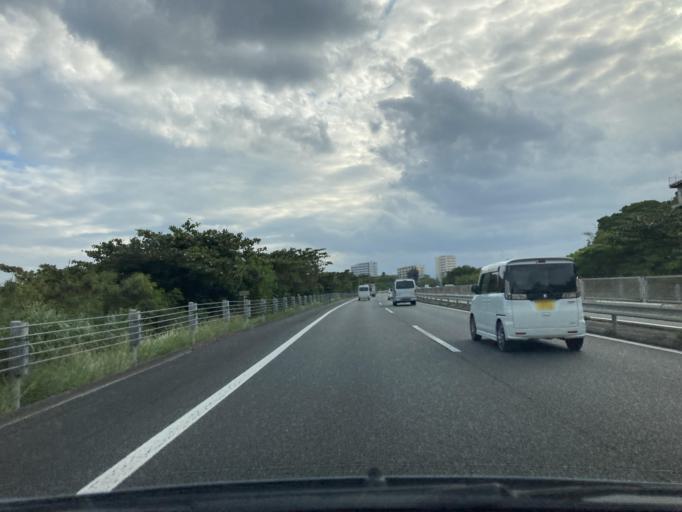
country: JP
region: Okinawa
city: Ginowan
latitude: 26.2625
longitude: 127.7724
